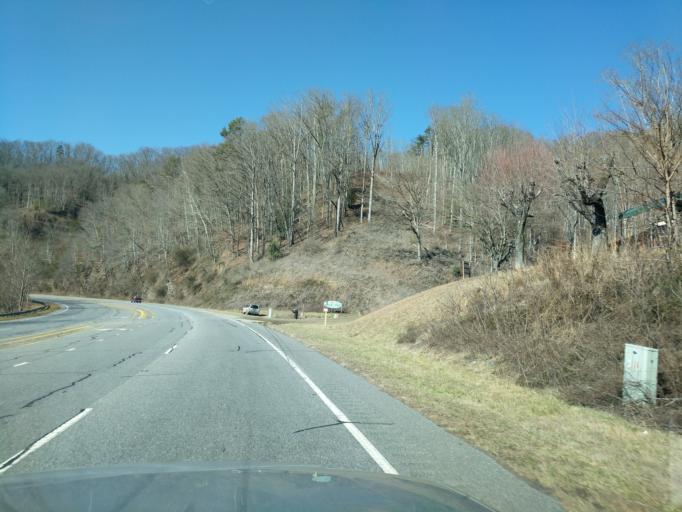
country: US
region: North Carolina
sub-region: Swain County
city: Cherokee
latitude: 35.4049
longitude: -83.2931
